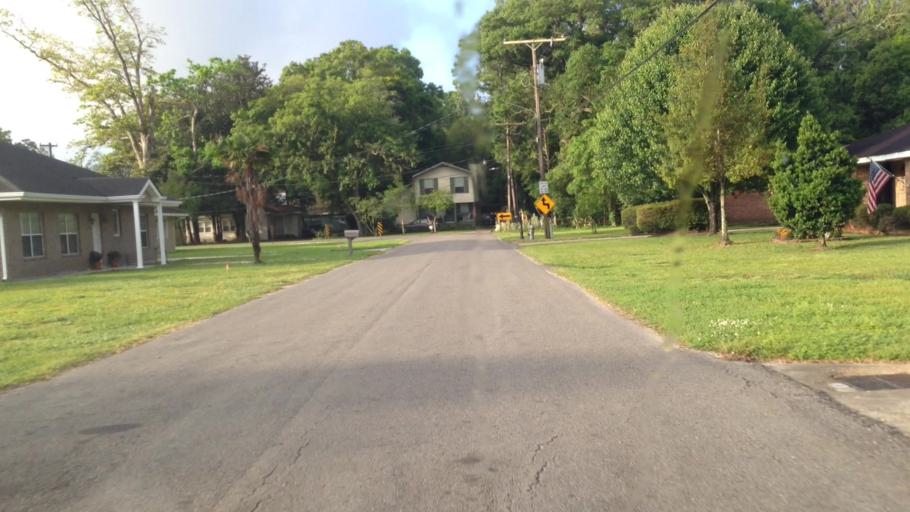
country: US
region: Louisiana
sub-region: Jefferson Parish
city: Jefferson
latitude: 29.9502
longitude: -90.1516
